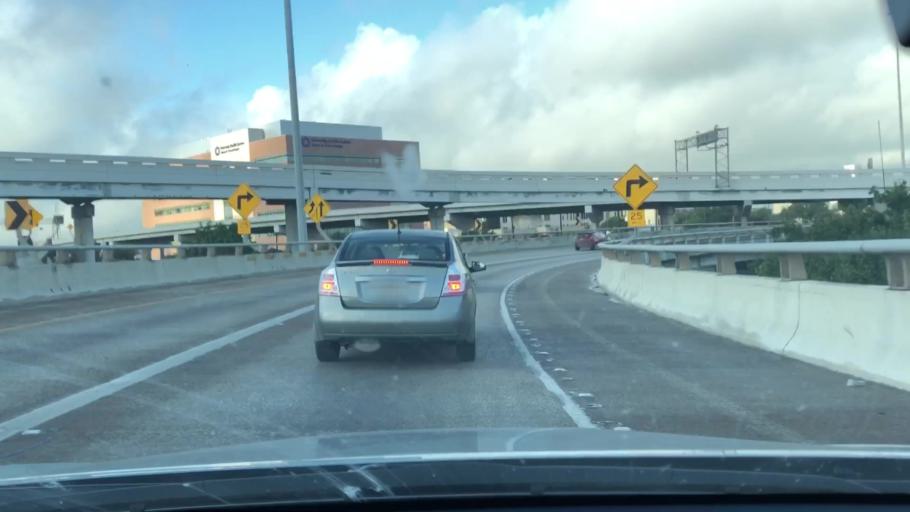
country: US
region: Texas
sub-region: Bexar County
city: San Antonio
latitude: 29.4327
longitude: -98.4999
